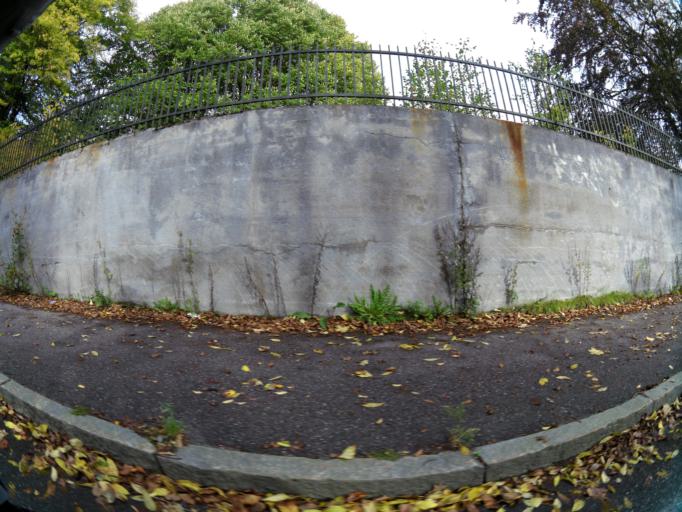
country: NO
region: Ostfold
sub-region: Fredrikstad
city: Fredrikstad
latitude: 59.2235
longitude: 10.9323
